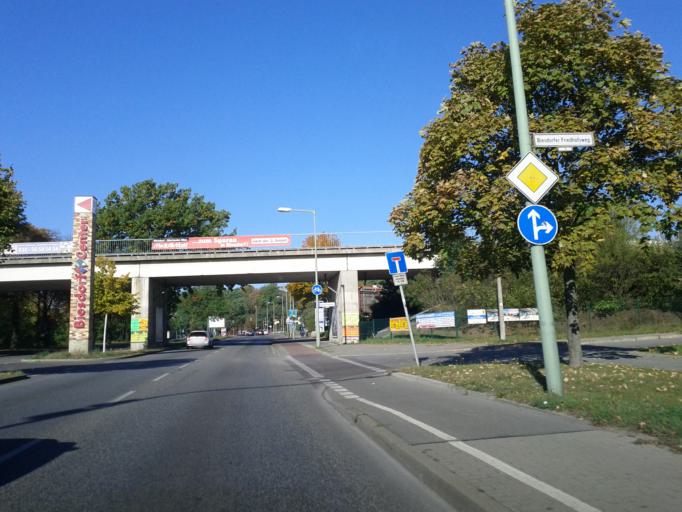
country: DE
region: Berlin
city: Biesdorf
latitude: 52.5076
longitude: 13.5648
